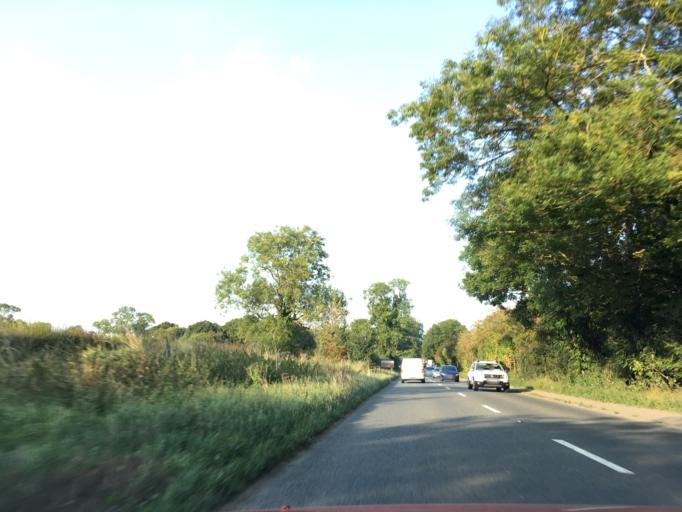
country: GB
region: England
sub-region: Gloucestershire
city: Bourton on the Water
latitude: 51.8977
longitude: -1.7530
